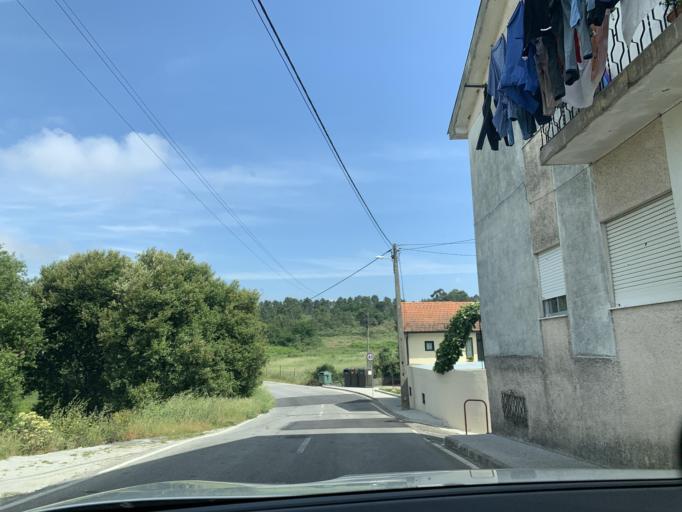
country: PT
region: Viseu
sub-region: Viseu
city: Viseu
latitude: 40.6398
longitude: -7.9355
